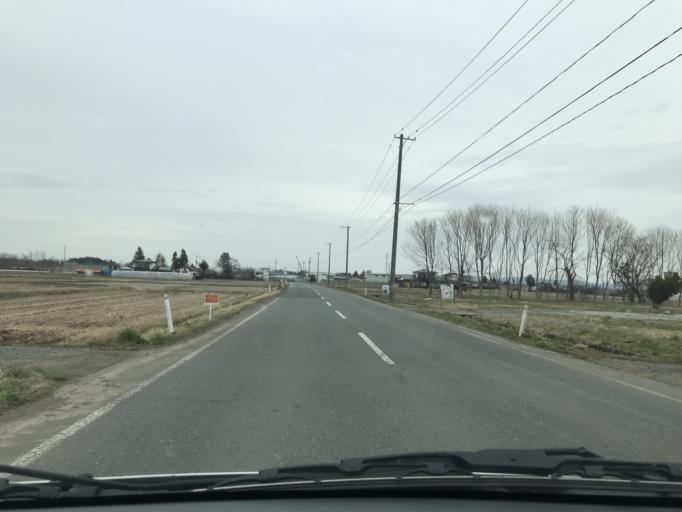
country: JP
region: Iwate
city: Mizusawa
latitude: 39.1744
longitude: 141.1136
